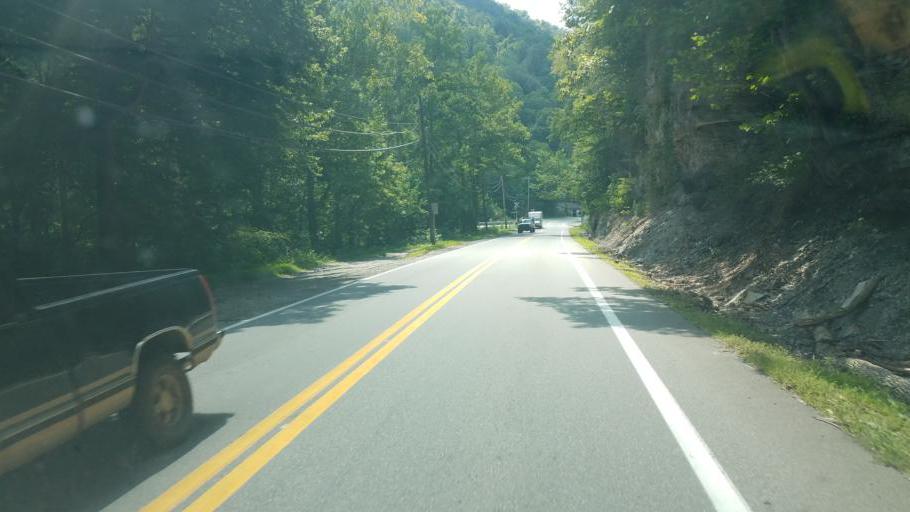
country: US
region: West Virginia
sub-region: Kanawha County
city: Chesapeake
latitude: 38.1734
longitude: -81.4500
